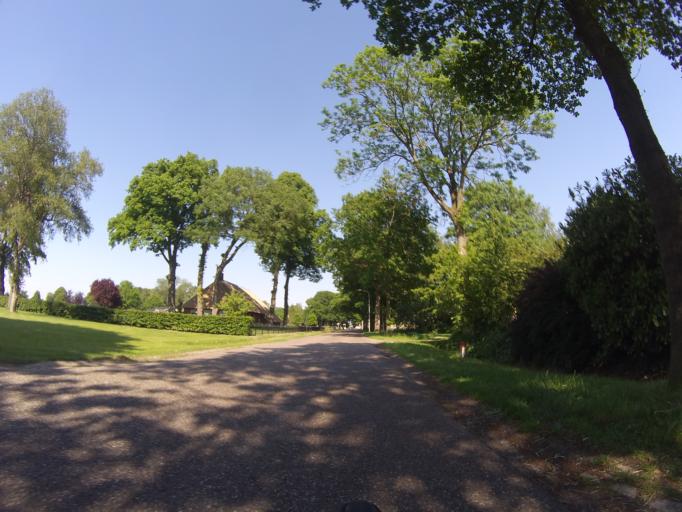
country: NL
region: Drenthe
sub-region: Gemeente Coevorden
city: Sleen
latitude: 52.7434
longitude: 6.8253
